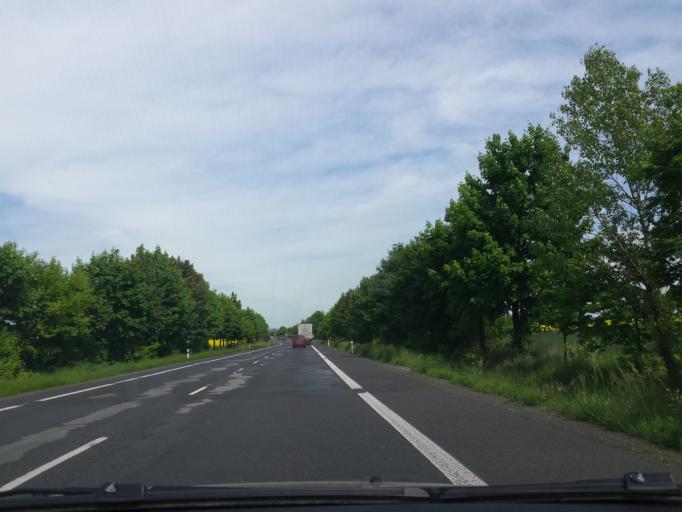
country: CZ
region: Central Bohemia
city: Luzec nad Vltavou
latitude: 50.3436
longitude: 14.4100
